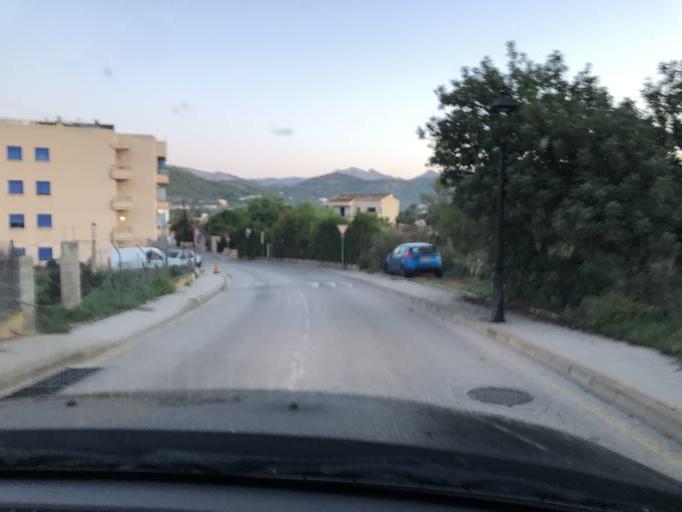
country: ES
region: Balearic Islands
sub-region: Illes Balears
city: Camp de Mar
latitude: 39.5444
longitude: 2.3927
